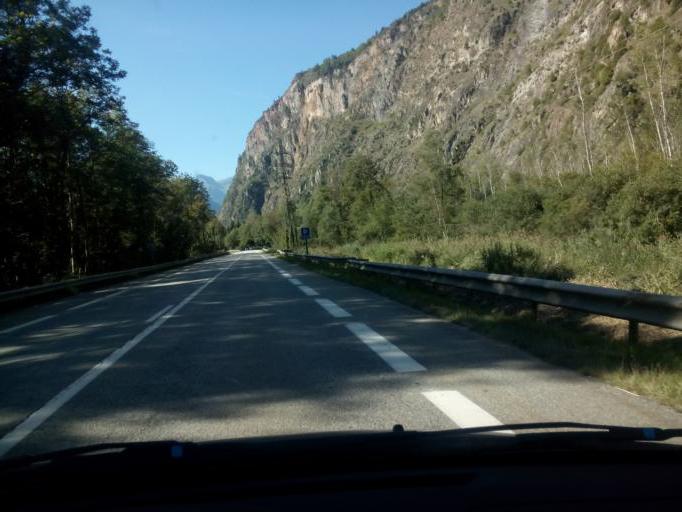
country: FR
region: Rhone-Alpes
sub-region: Departement de l'Isere
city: Huez
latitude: 45.0441
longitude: 6.0581
